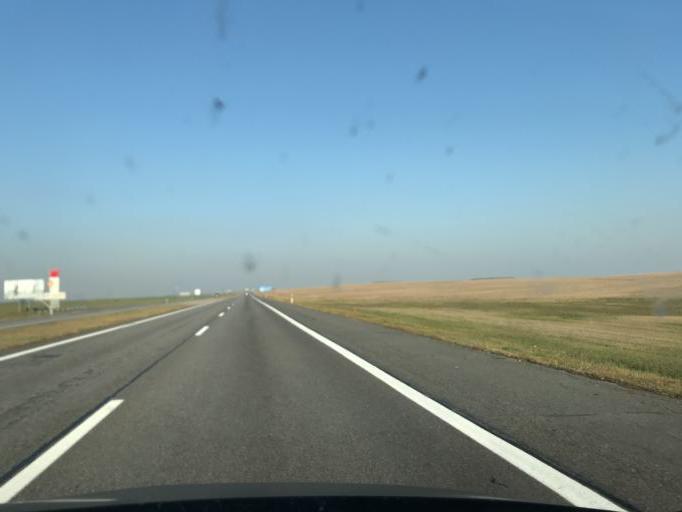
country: BY
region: Minsk
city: Snow
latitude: 53.3139
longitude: 26.3970
